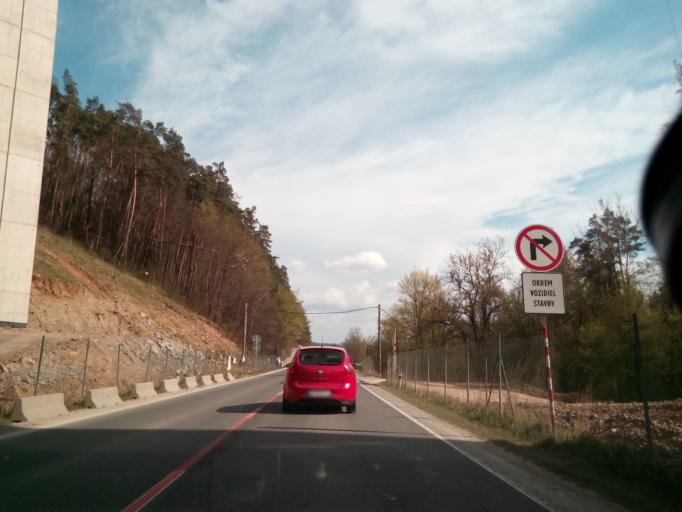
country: SK
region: Presovsky
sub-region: Okres Presov
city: Levoca
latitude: 49.0066
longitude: 20.6363
